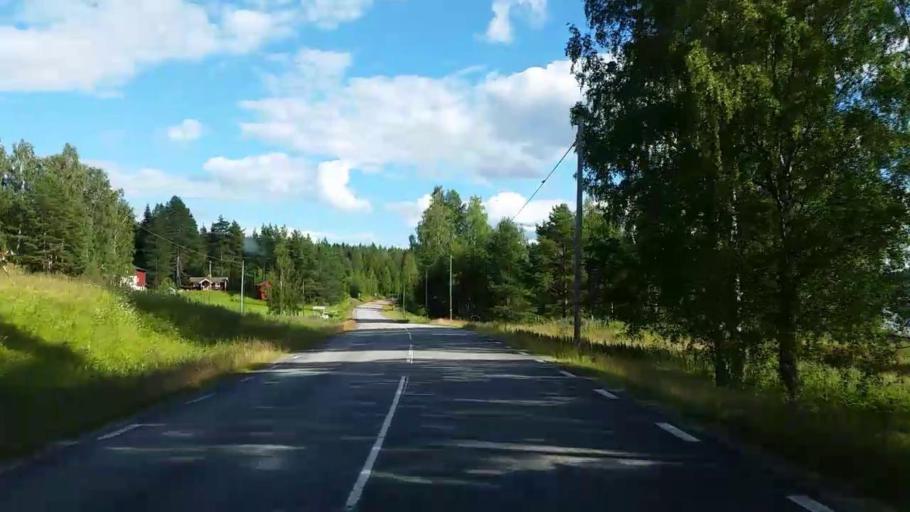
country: SE
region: Vaesternorrland
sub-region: Ange Kommun
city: Ange
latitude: 62.1545
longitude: 15.6777
